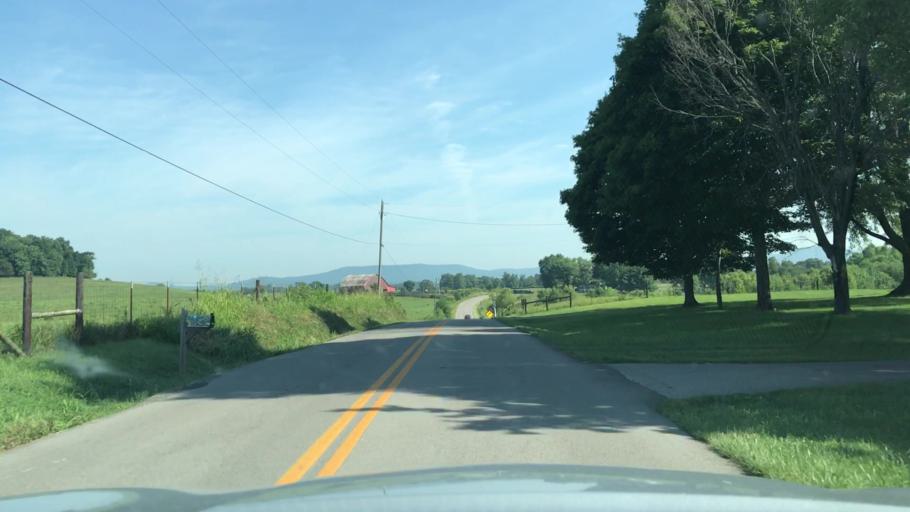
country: US
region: Tennessee
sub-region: Pickett County
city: Byrdstown
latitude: 36.6311
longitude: -85.0852
